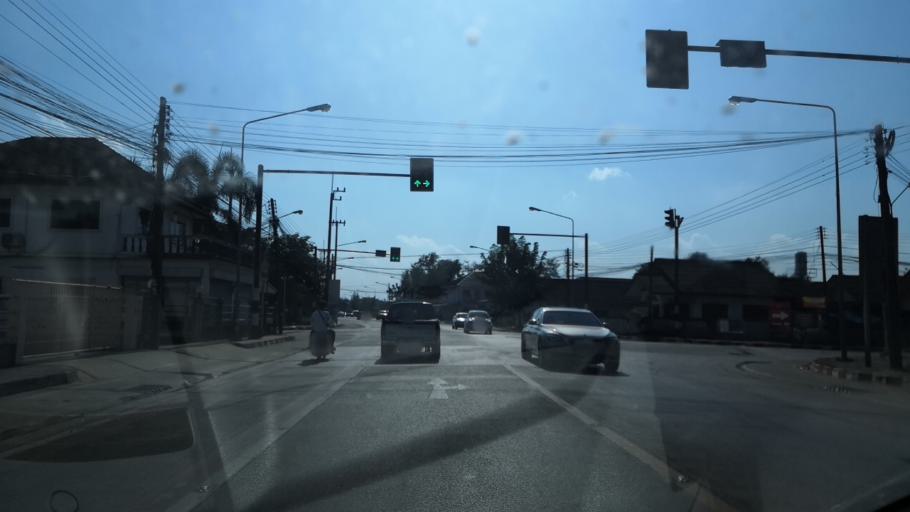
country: TH
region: Chiang Rai
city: Chiang Rai
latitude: 19.9339
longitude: 99.8413
